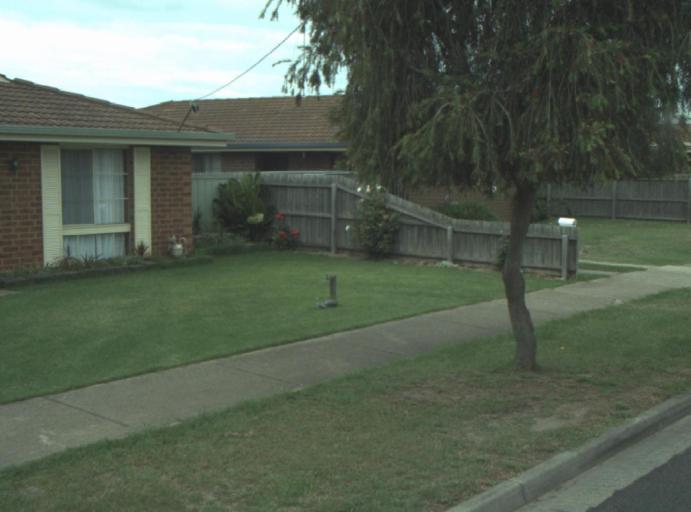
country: AU
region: Victoria
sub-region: Greater Geelong
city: Breakwater
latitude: -38.2065
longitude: 144.3494
